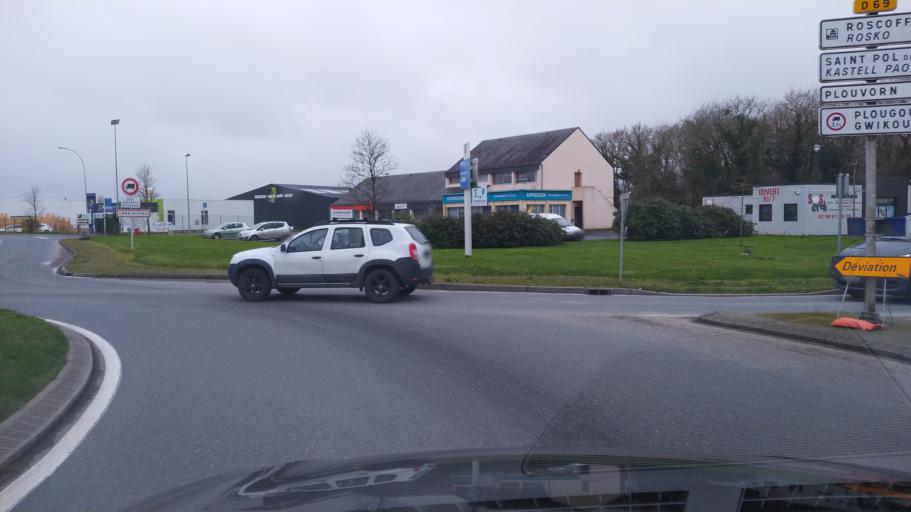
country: FR
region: Brittany
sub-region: Departement du Finistere
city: Landivisiau
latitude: 48.5224
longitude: -4.0607
